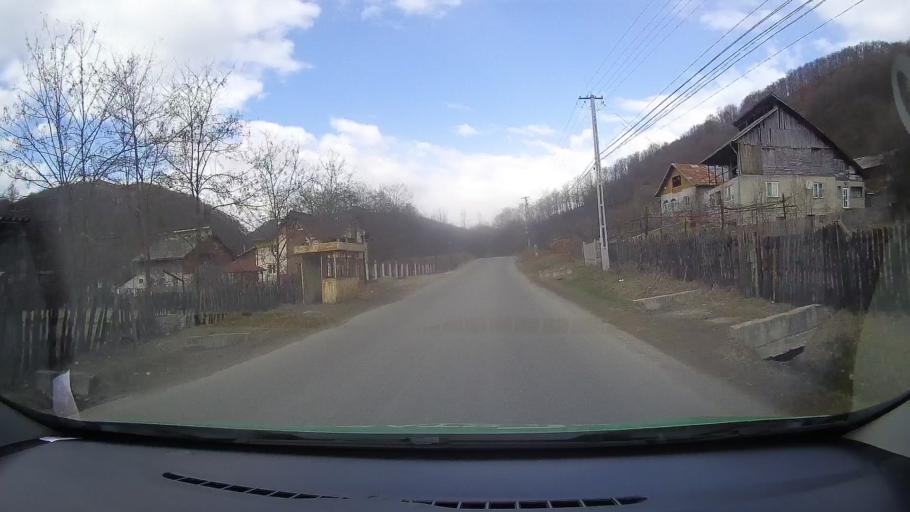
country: RO
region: Dambovita
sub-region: Comuna Varfuri
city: Varfuri
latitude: 45.0783
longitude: 25.5168
